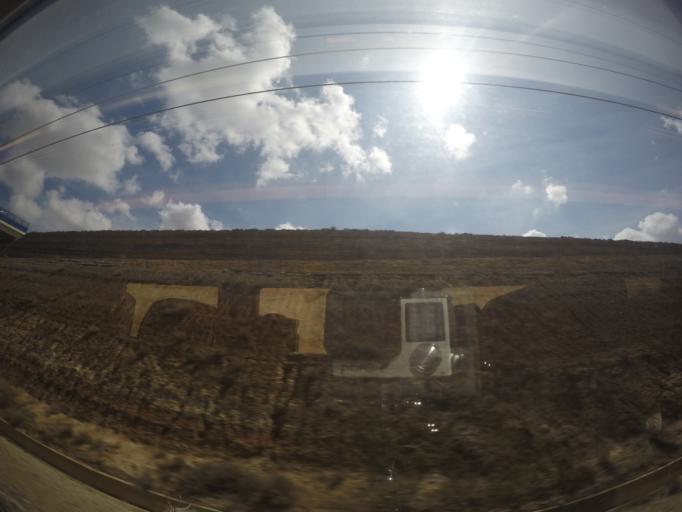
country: ES
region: Aragon
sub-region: Provincia de Huesca
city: Candasnos
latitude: 41.5750
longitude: 0.1146
